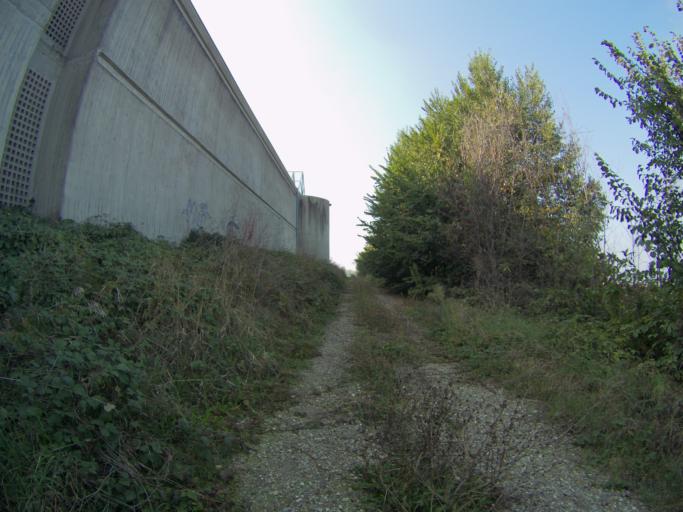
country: IT
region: Emilia-Romagna
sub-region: Provincia di Reggio Emilia
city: Forche
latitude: 44.6630
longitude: 10.5856
